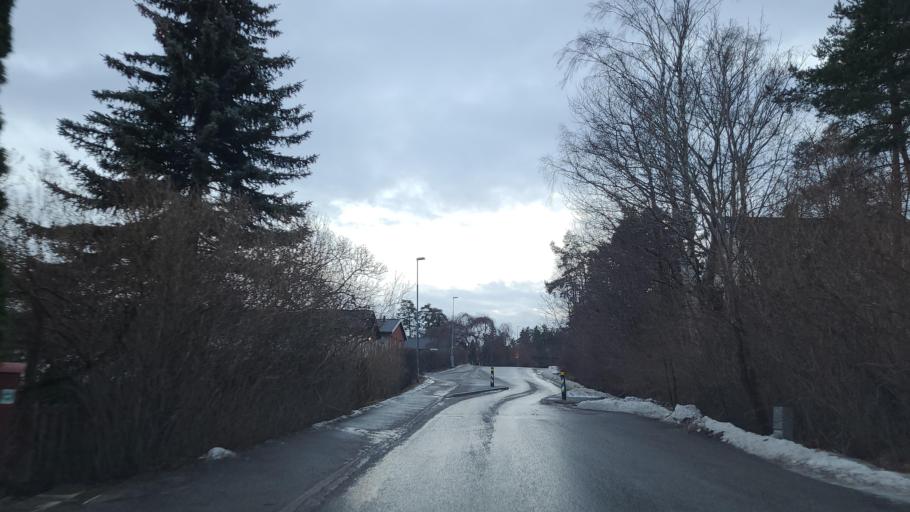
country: SE
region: Stockholm
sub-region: Vallentuna Kommun
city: Vallentuna
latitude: 59.5149
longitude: 18.0632
